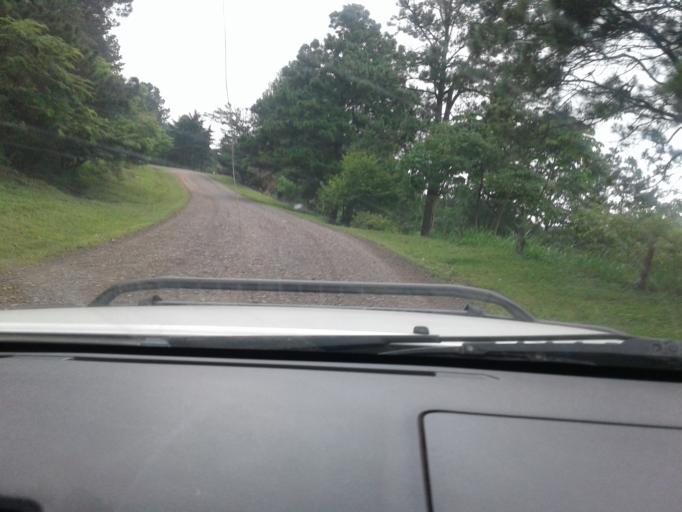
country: NI
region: Matagalpa
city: San Ramon
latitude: 12.9105
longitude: -85.7802
